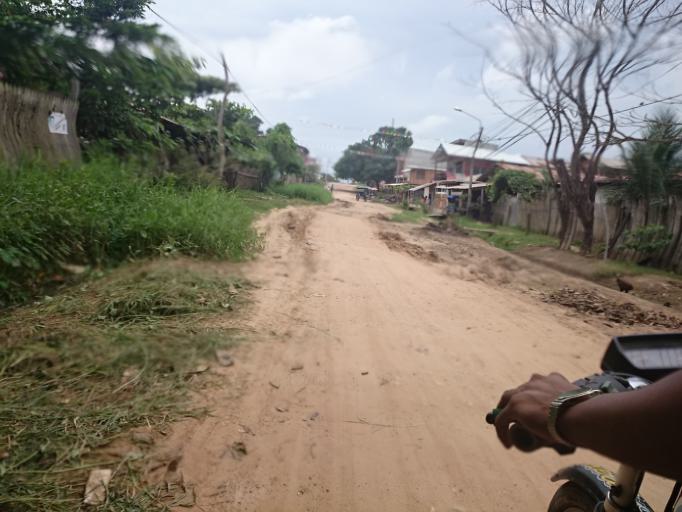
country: PE
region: Ucayali
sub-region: Provincia de Coronel Portillo
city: Pucallpa
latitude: -8.3745
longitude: -74.5527
